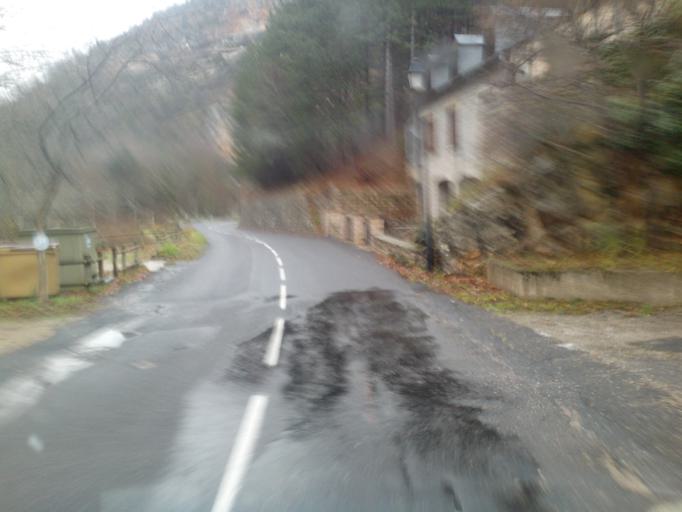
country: FR
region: Languedoc-Roussillon
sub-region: Departement de la Lozere
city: Chanac
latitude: 44.3604
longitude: 3.4077
